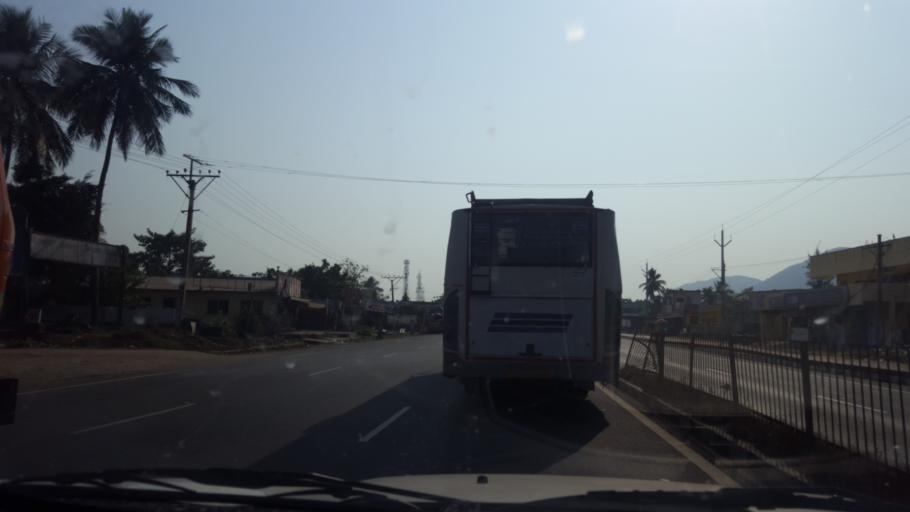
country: IN
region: Andhra Pradesh
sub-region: Vishakhapatnam
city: Elamanchili
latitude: 17.6370
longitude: 82.8967
